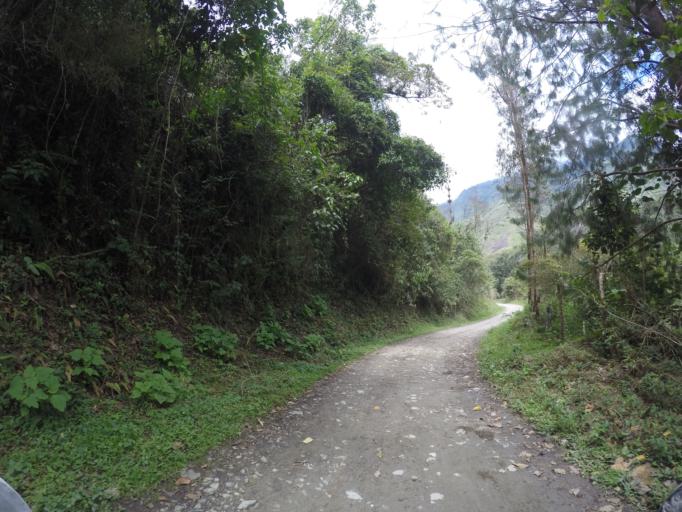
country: CO
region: Tolima
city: Cajamarca
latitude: 4.5262
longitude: -75.4078
